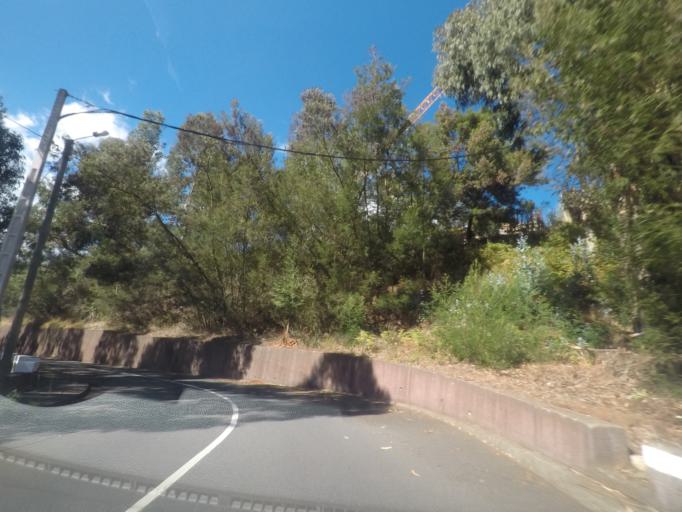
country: PT
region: Madeira
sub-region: Ribeira Brava
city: Campanario
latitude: 32.6844
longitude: -17.0404
